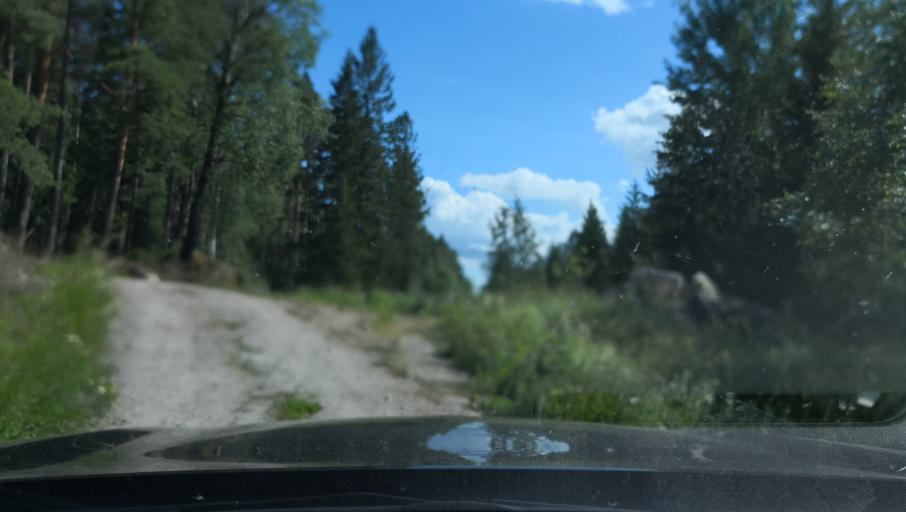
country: SE
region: Vaestmanland
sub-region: Kungsors Kommun
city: Kungsoer
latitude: 59.3432
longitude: 16.0589
